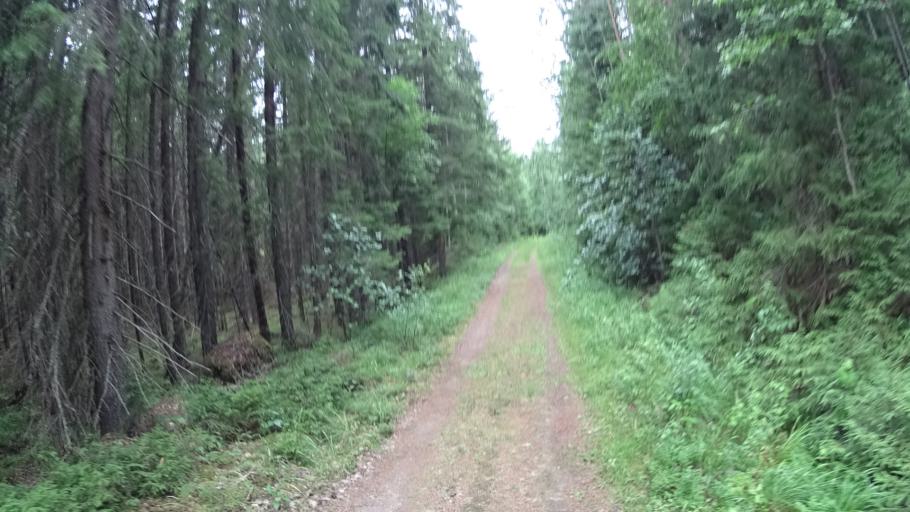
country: FI
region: Southern Savonia
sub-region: Mikkeli
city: Maentyharju
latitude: 61.1869
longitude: 26.8275
